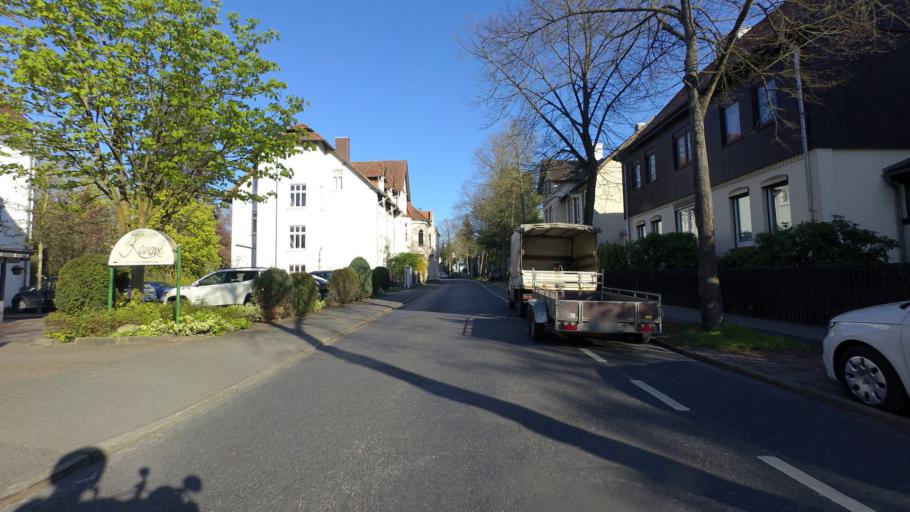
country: DE
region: Lower Saxony
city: Celle
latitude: 52.6291
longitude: 10.0754
